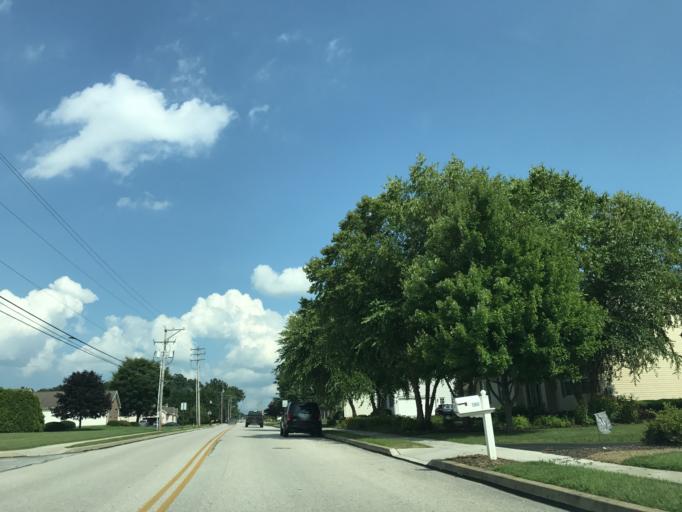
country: US
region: Pennsylvania
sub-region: York County
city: Pennville
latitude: 39.7699
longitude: -76.9867
